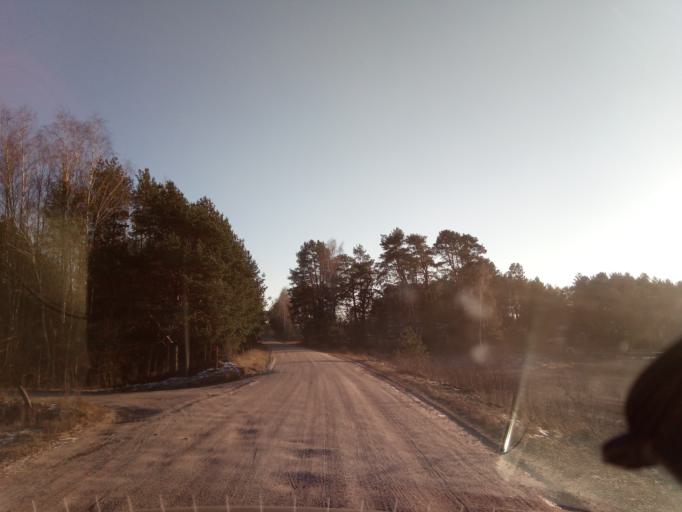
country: LT
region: Alytaus apskritis
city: Druskininkai
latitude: 53.9747
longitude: 23.9454
